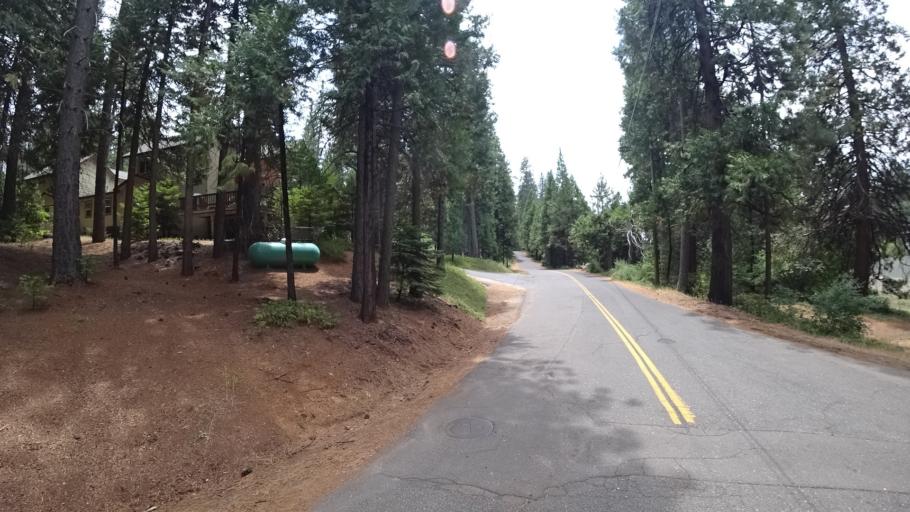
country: US
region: California
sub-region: Calaveras County
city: Arnold
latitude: 38.2419
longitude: -120.3599
